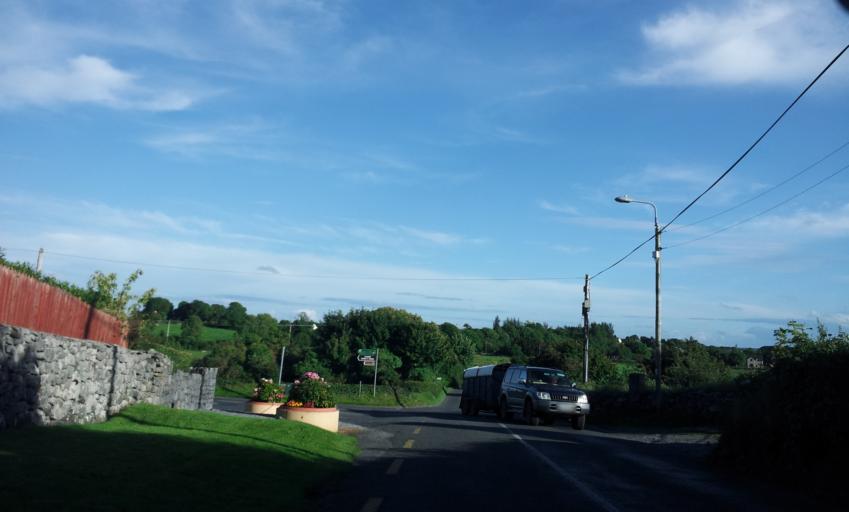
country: IE
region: Munster
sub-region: An Clar
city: Ennis
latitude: 52.9701
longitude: -9.0858
